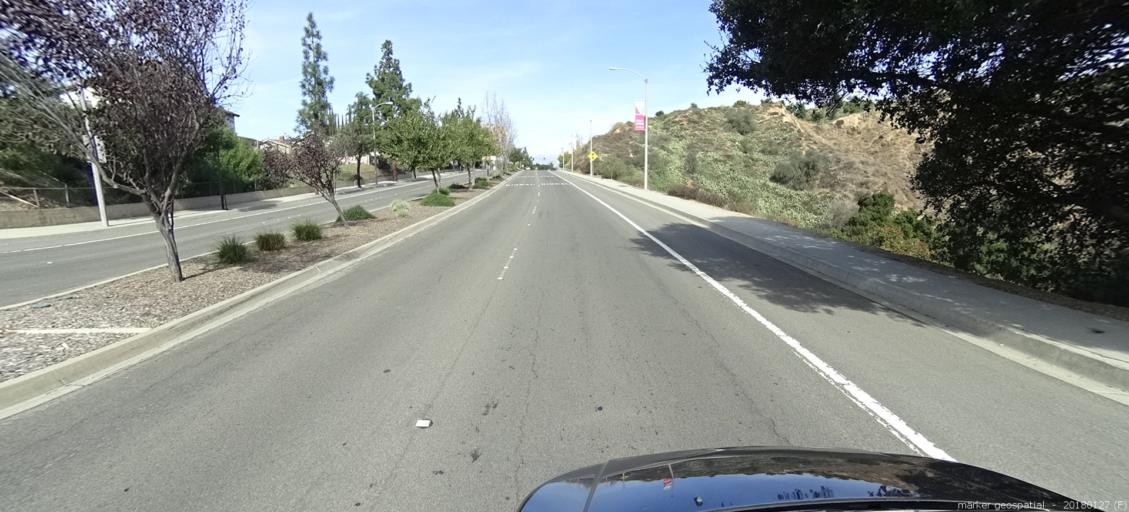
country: US
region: California
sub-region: Los Angeles County
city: Diamond Bar
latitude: 34.0073
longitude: -117.8081
